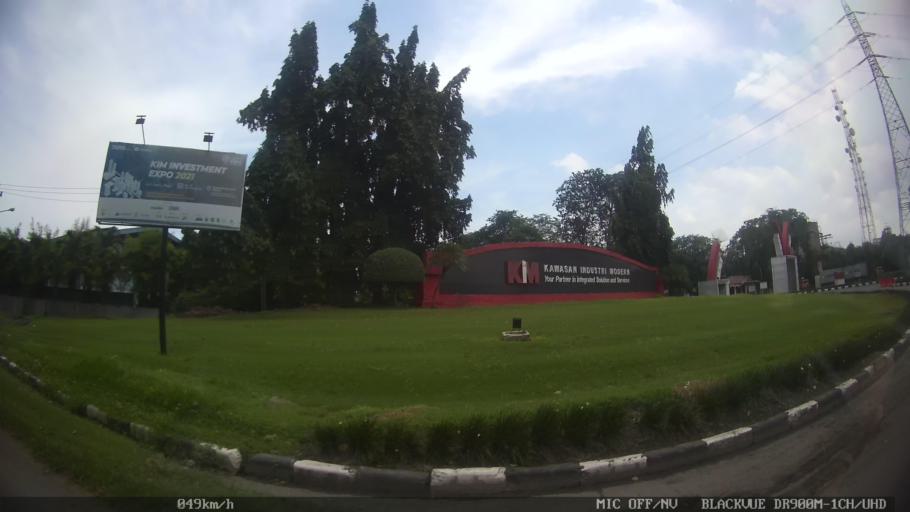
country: ID
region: North Sumatra
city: Labuhan Deli
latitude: 3.6740
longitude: 98.6834
